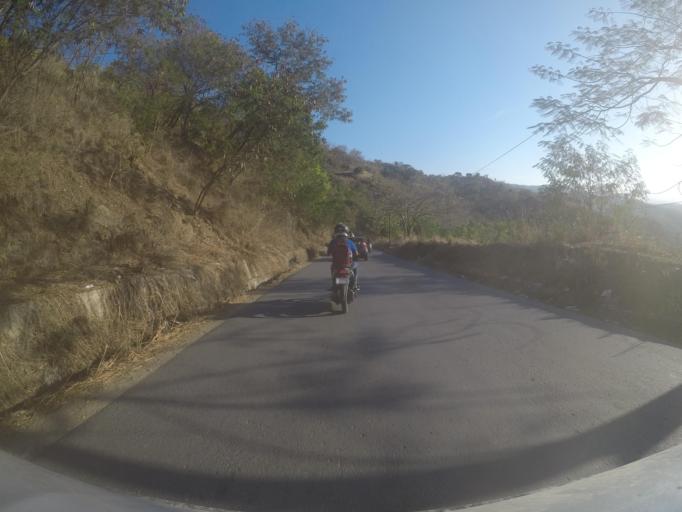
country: TL
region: Dili
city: Dili
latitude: -8.5671
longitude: 125.6312
